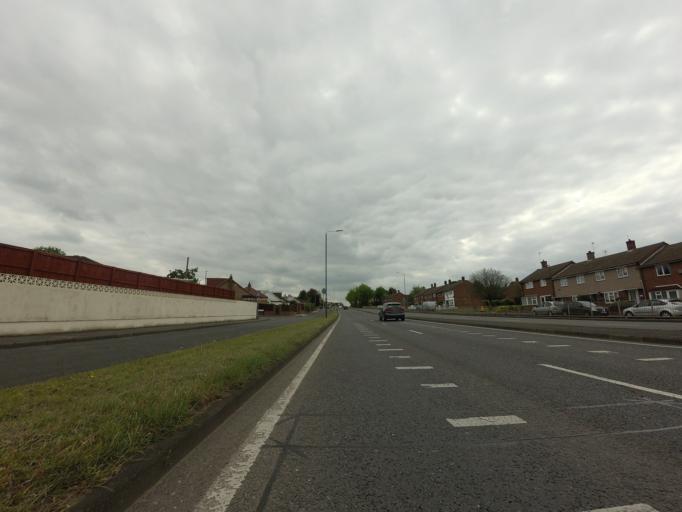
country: GB
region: England
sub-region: Greater London
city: Bexley
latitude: 51.4187
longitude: 0.1315
